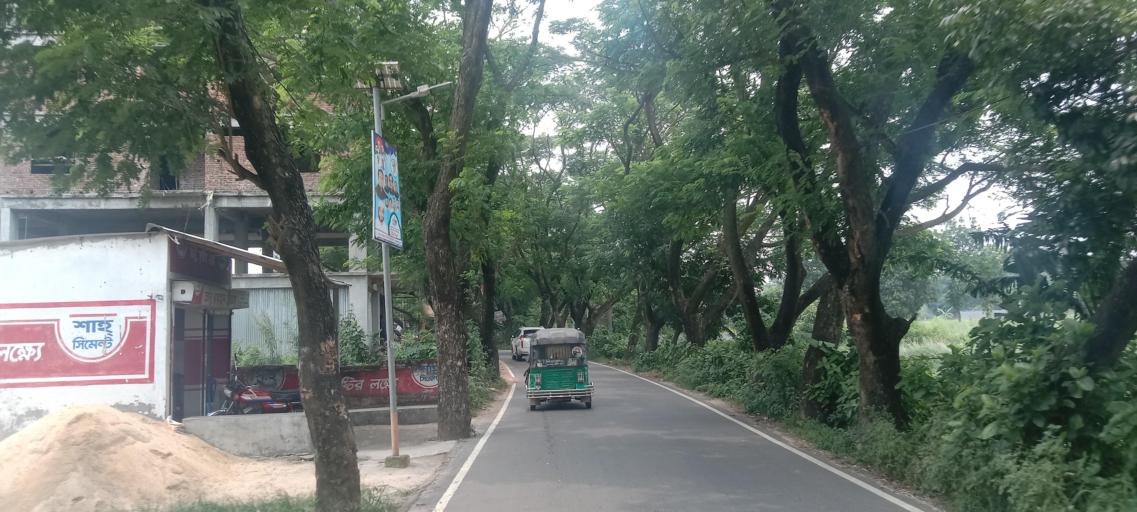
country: BD
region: Dhaka
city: Azimpur
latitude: 23.7144
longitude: 90.3448
